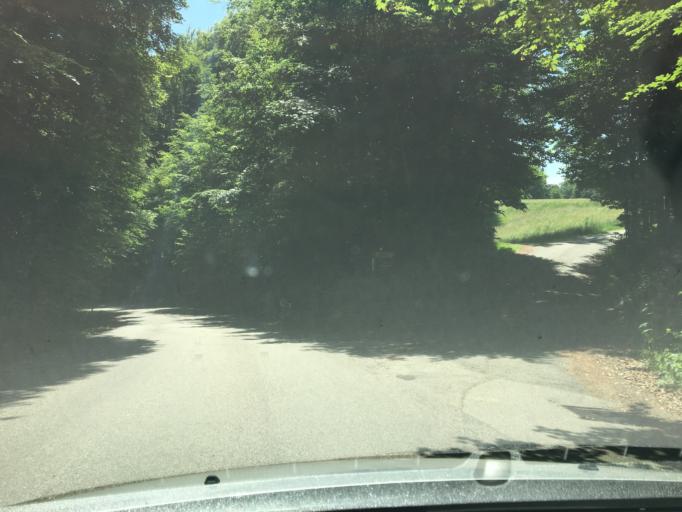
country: DE
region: Bavaria
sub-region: Upper Bavaria
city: Unterneukirchen
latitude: 48.1560
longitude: 12.6469
